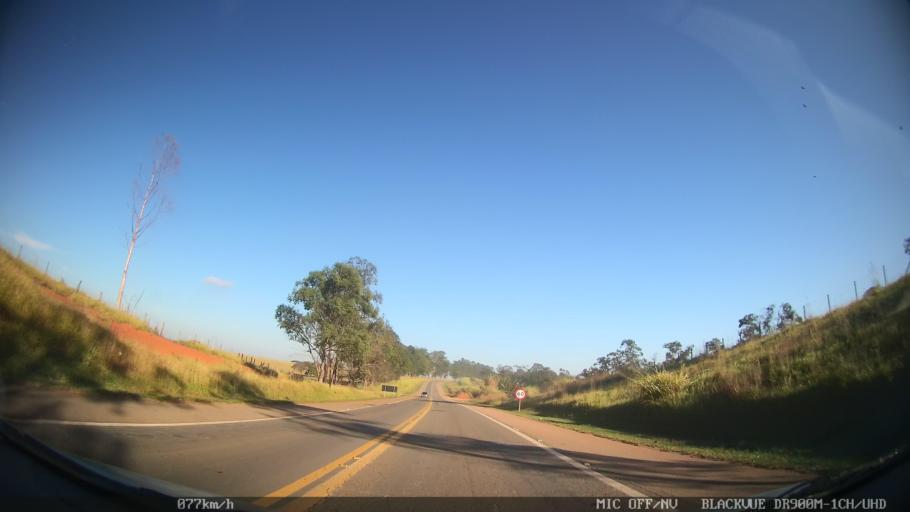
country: BR
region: Sao Paulo
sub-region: Itupeva
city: Itupeva
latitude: -23.0490
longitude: -47.0868
